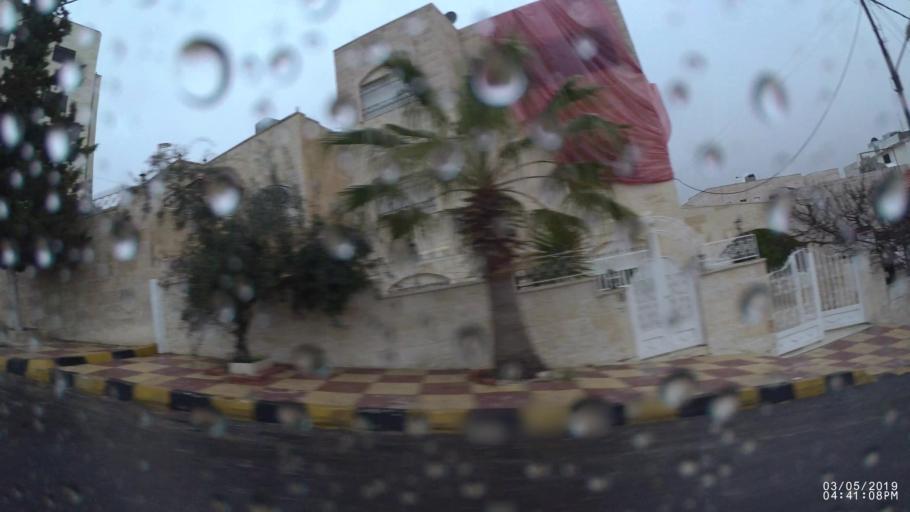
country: JO
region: Amman
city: Amman
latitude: 31.9991
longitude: 35.9663
